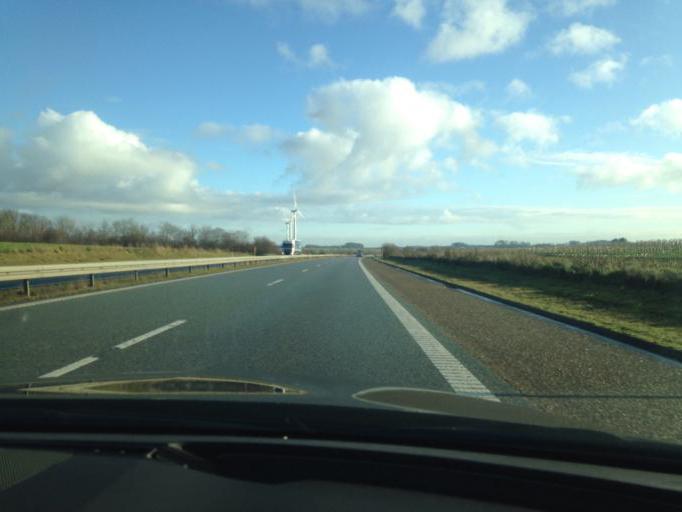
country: DK
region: South Denmark
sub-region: Vejen Kommune
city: Brorup
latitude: 55.5096
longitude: 8.9879
